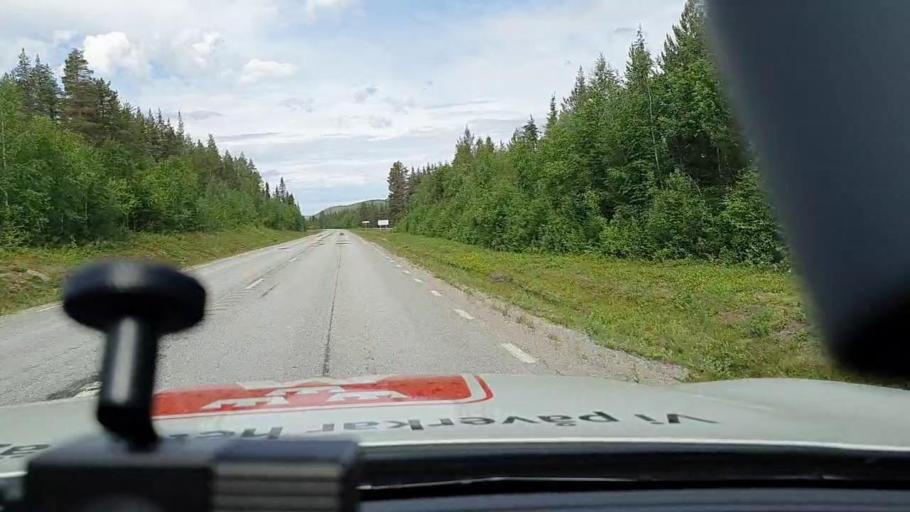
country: SE
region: Norrbotten
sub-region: Jokkmokks Kommun
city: Jokkmokk
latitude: 66.5515
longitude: 20.1188
